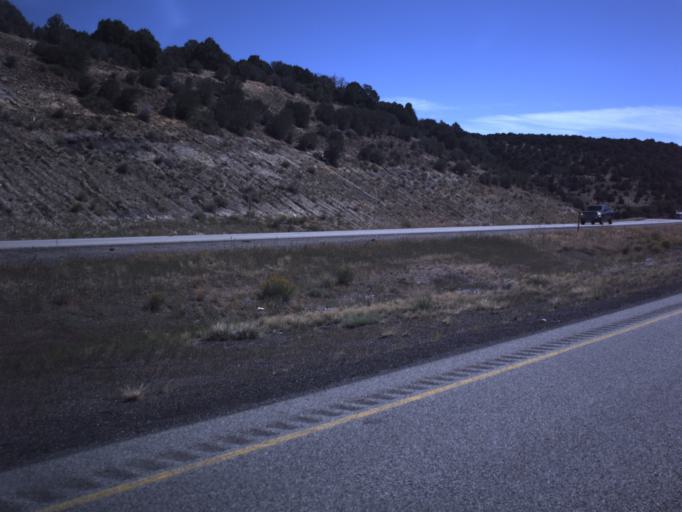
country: US
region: Utah
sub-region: Wayne County
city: Loa
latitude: 38.7793
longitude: -111.4843
